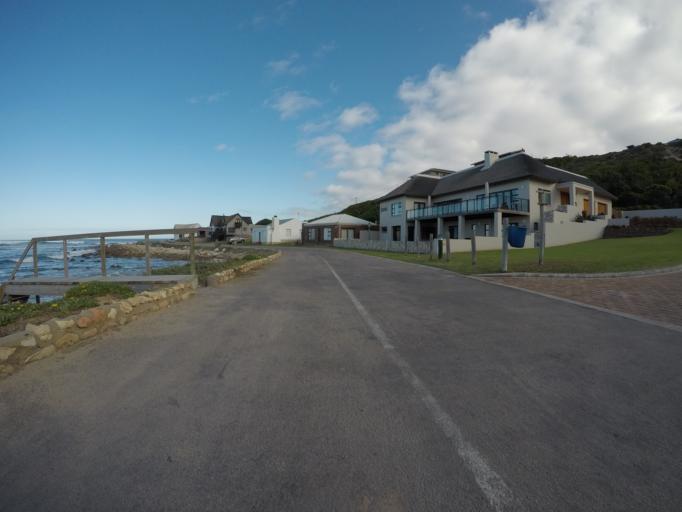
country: ZA
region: Western Cape
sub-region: Eden District Municipality
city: Riversdale
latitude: -34.4308
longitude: 21.3351
